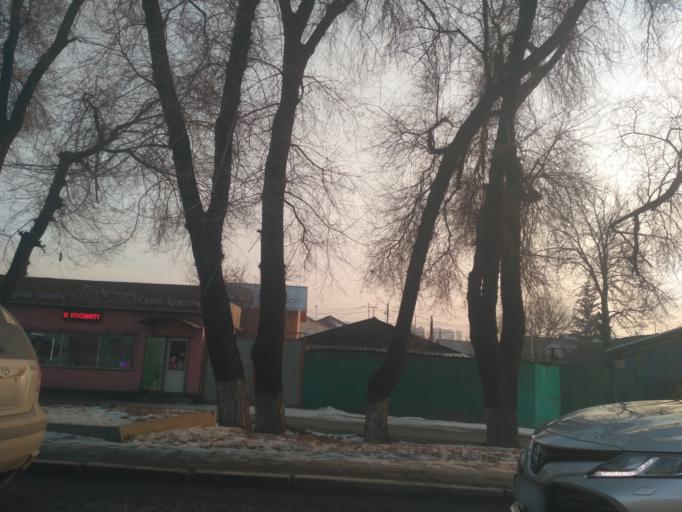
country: KZ
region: Almaty Qalasy
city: Almaty
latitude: 43.2506
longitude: 76.8516
